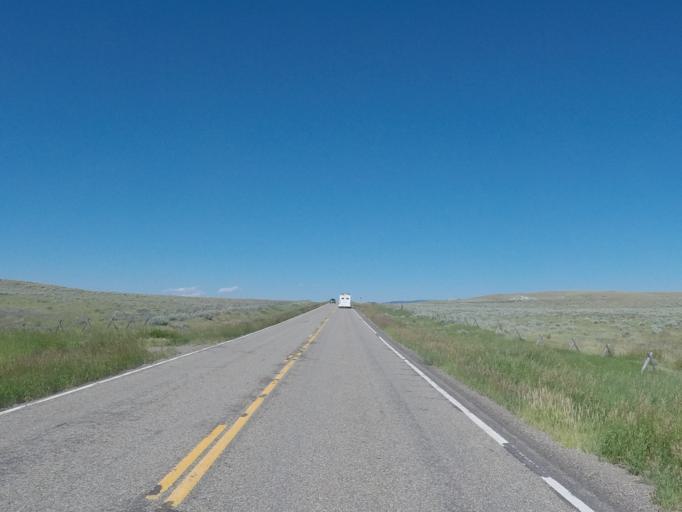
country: US
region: Montana
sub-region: Meagher County
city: White Sulphur Springs
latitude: 46.3742
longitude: -110.9958
